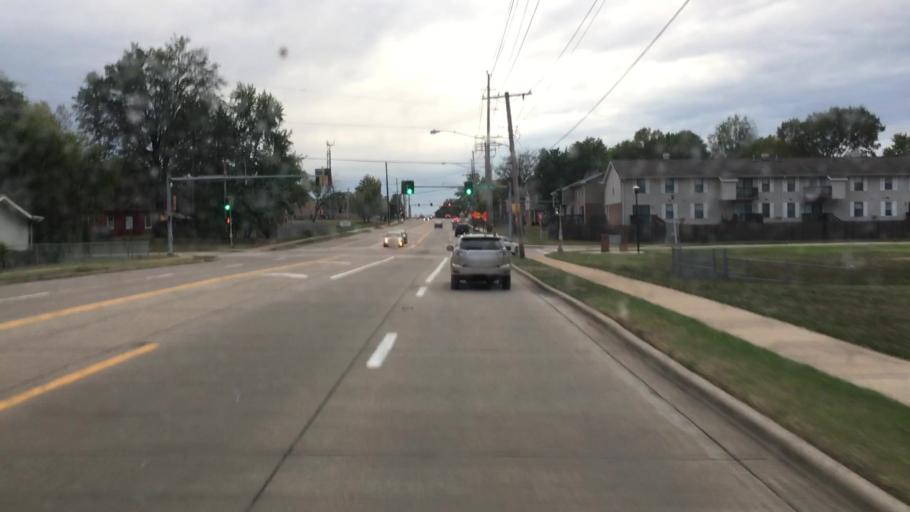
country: US
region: Missouri
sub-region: Saint Louis County
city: Florissant
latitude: 38.8214
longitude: -90.3402
